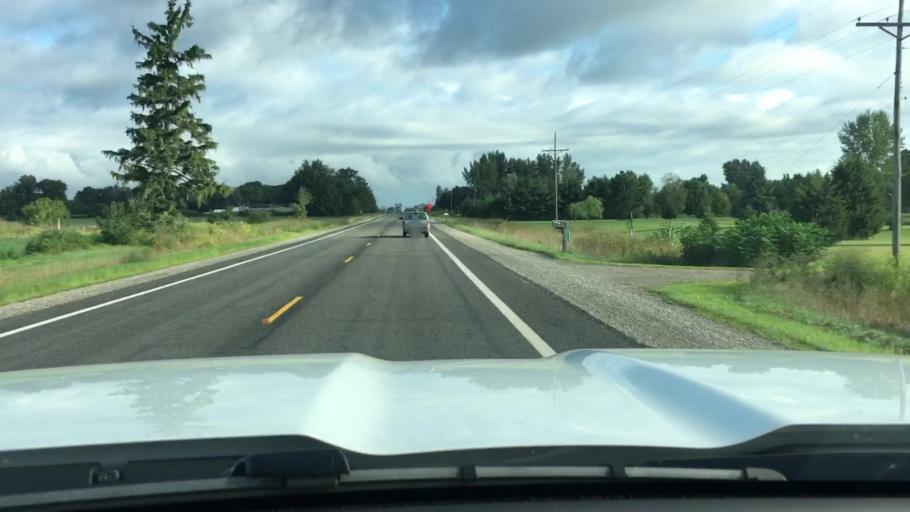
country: US
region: Michigan
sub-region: Tuscola County
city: Caro
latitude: 43.3951
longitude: -83.3835
